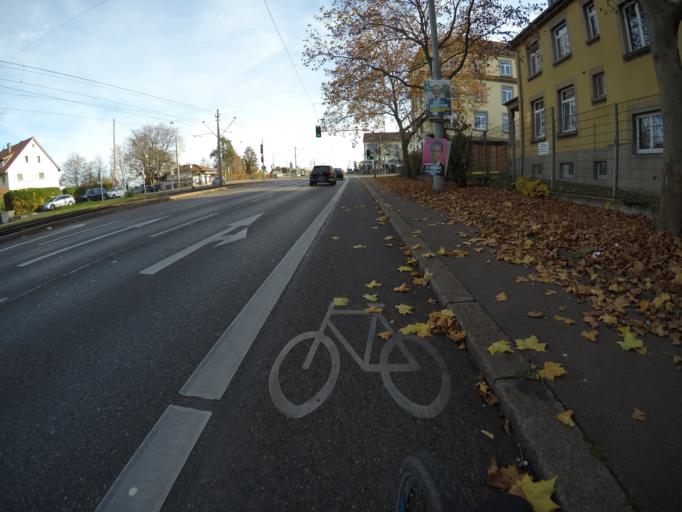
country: DE
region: Baden-Wuerttemberg
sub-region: Regierungsbezirk Stuttgart
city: Fellbach
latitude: 48.8097
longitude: 9.2520
